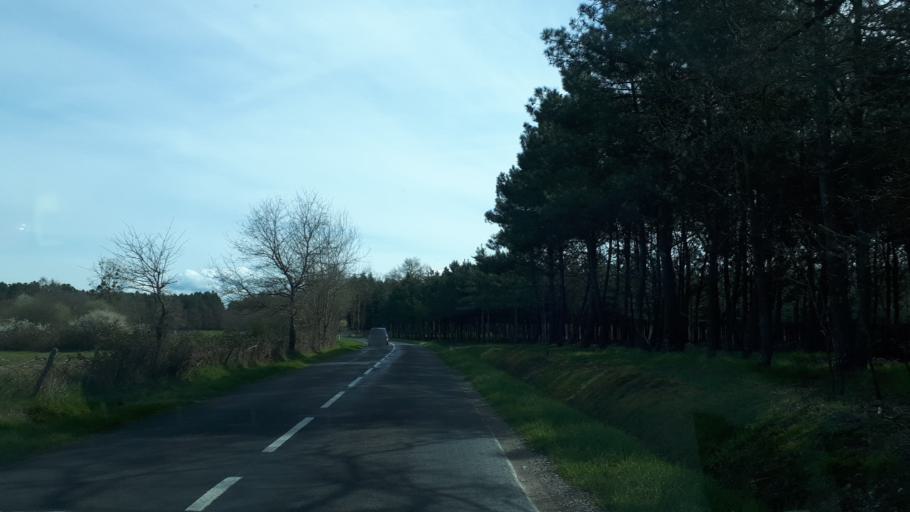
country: FR
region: Pays de la Loire
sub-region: Departement de la Sarthe
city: Saint-Ouen-en-Belin
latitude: 47.8254
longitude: 0.1860
